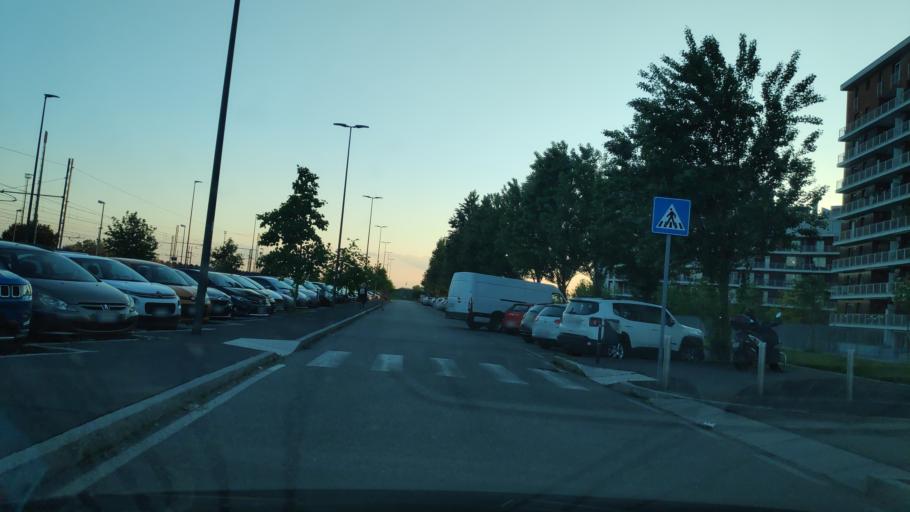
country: IT
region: Lombardy
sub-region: Citta metropolitana di Milano
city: Segrate
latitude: 45.4809
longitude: 9.2981
